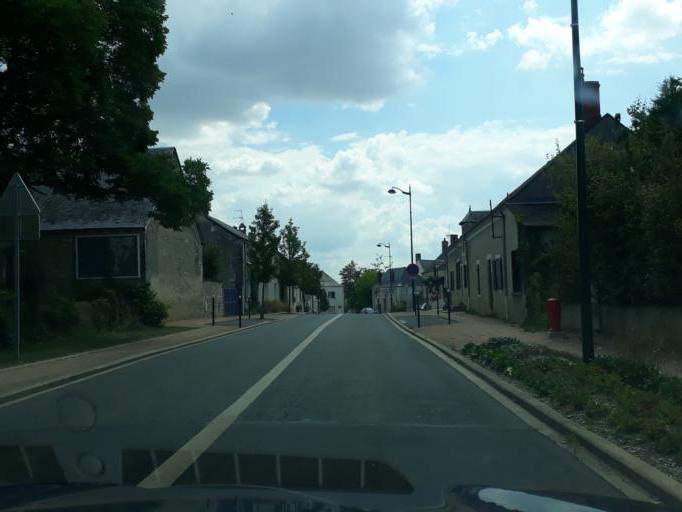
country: FR
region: Centre
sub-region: Departement du Cher
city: Sainte-Solange
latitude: 47.0455
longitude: 2.5607
